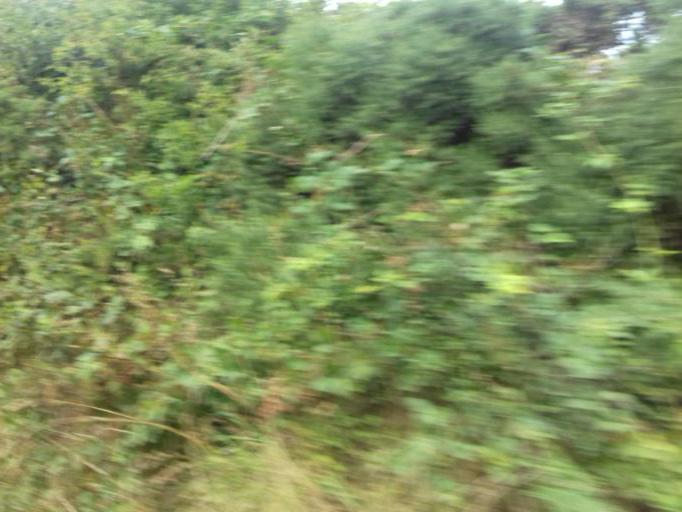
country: IE
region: Leinster
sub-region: Loch Garman
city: Bunclody
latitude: 52.6511
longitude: -6.7412
